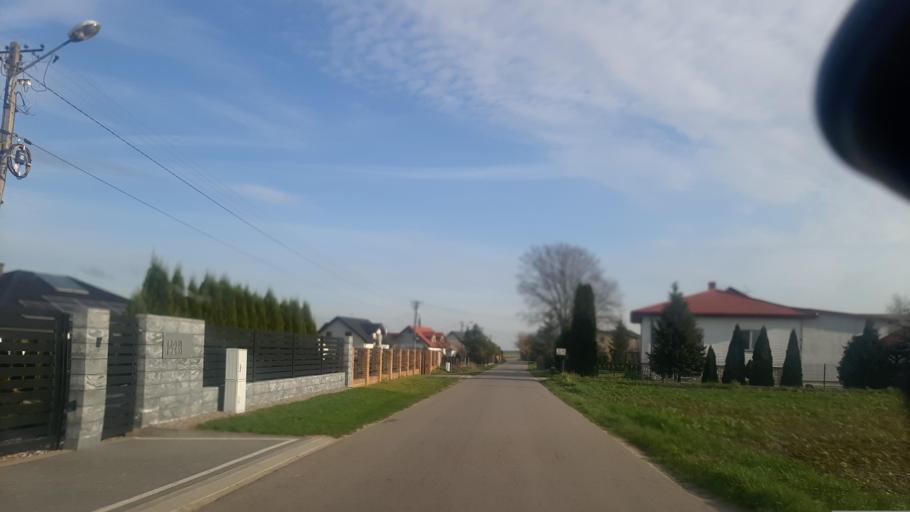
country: PL
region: Lublin Voivodeship
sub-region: Powiat lubelski
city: Garbow
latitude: 51.3842
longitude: 22.3401
